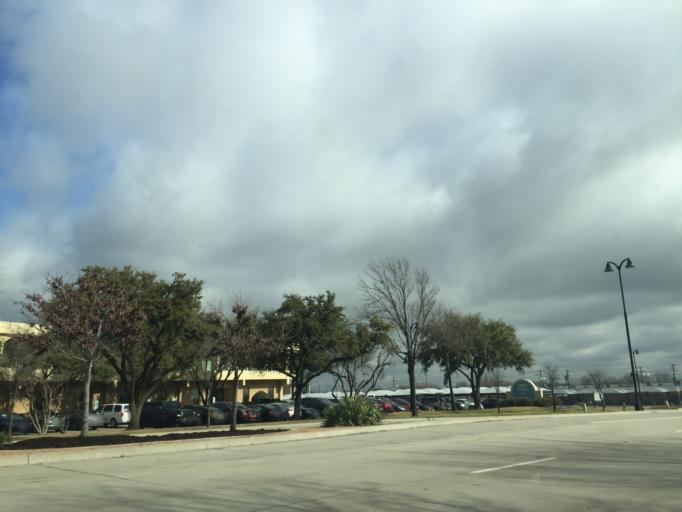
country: US
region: Texas
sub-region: Tarrant County
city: Arlington
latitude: 32.7644
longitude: -97.0879
